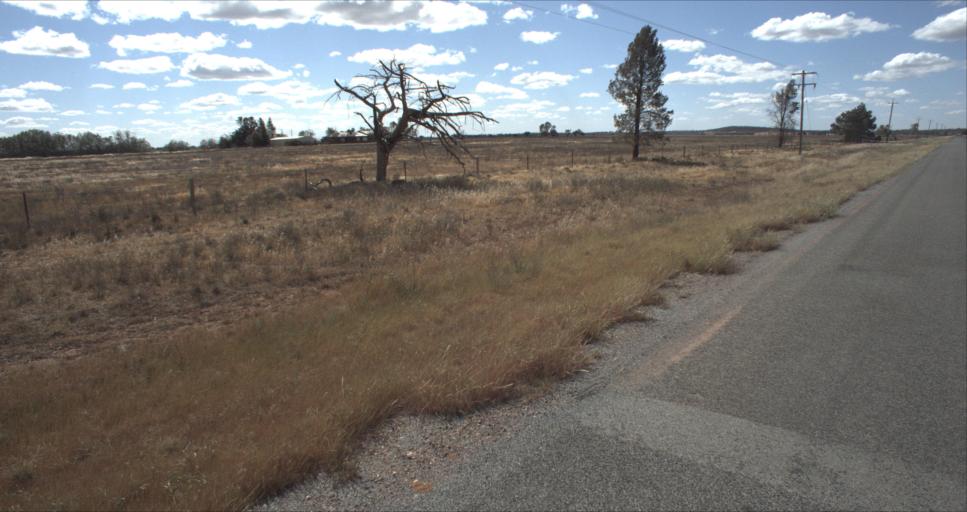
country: AU
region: New South Wales
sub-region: Leeton
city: Leeton
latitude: -34.4587
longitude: 146.2532
